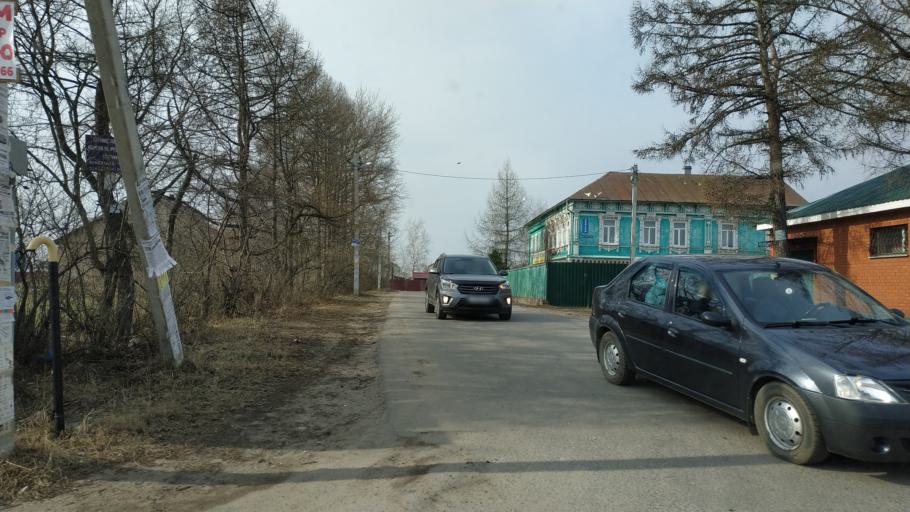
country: RU
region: Moskovskaya
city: Beloozerskiy
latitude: 55.4365
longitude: 38.4856
